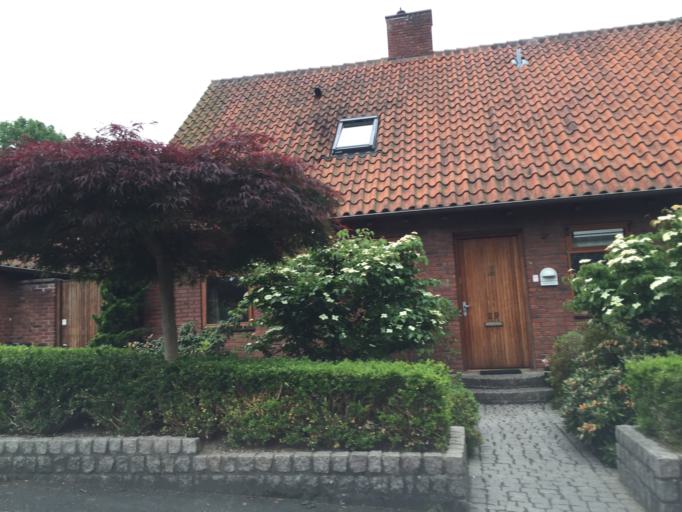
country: DK
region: Capital Region
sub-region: Lyngby-Tarbaek Kommune
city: Kongens Lyngby
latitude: 55.7690
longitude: 12.5283
